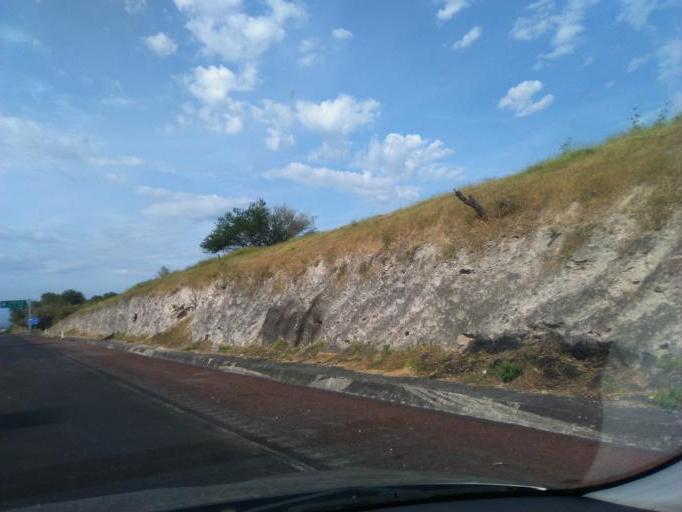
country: MX
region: Morelos
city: Puente de Ixtla
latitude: 18.6420
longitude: -99.2954
